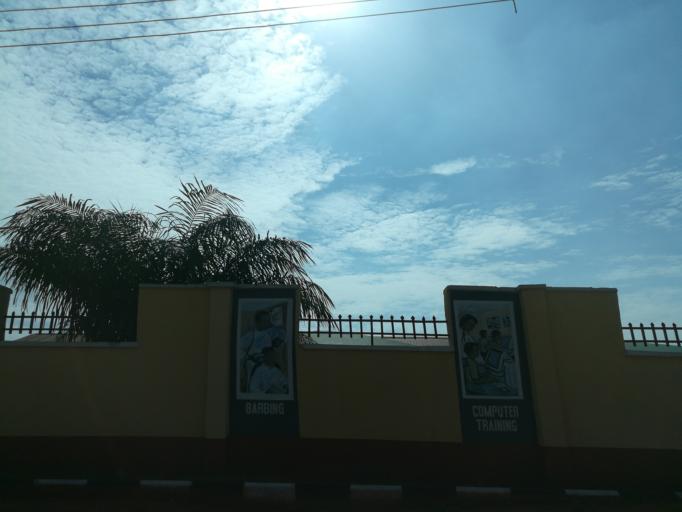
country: NG
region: Lagos
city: Ikorodu
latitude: 6.6023
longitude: 3.5056
